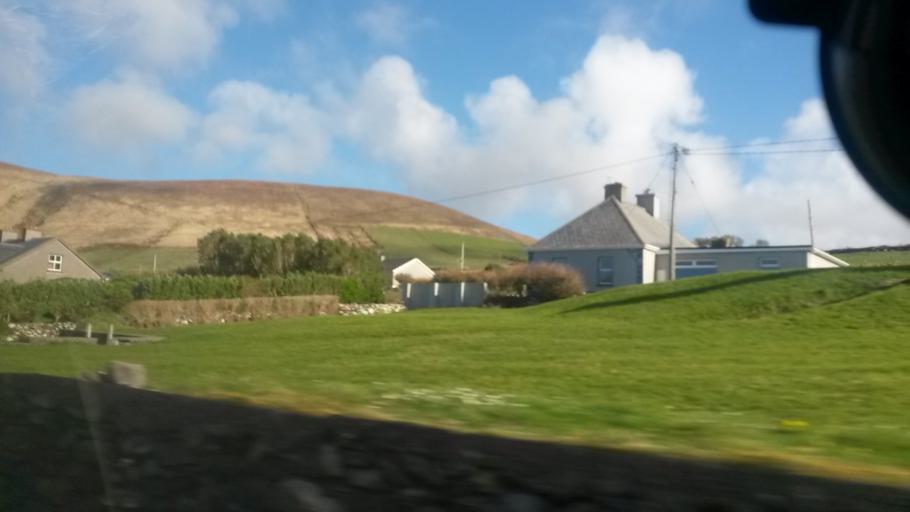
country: IE
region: Munster
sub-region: Ciarrai
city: Dingle
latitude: 52.1507
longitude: -10.4604
